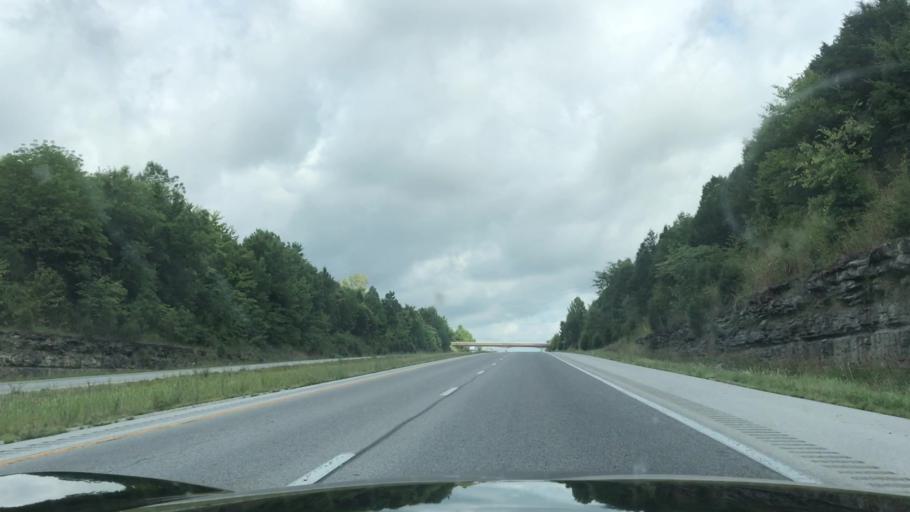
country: US
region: Kentucky
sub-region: Warren County
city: Bowling Green
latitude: 37.0243
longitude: -86.5309
